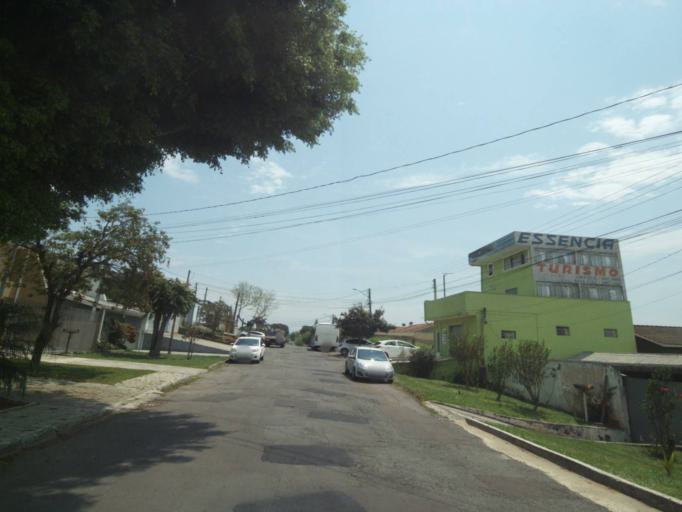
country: BR
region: Parana
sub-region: Pinhais
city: Pinhais
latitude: -25.4172
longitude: -49.2028
